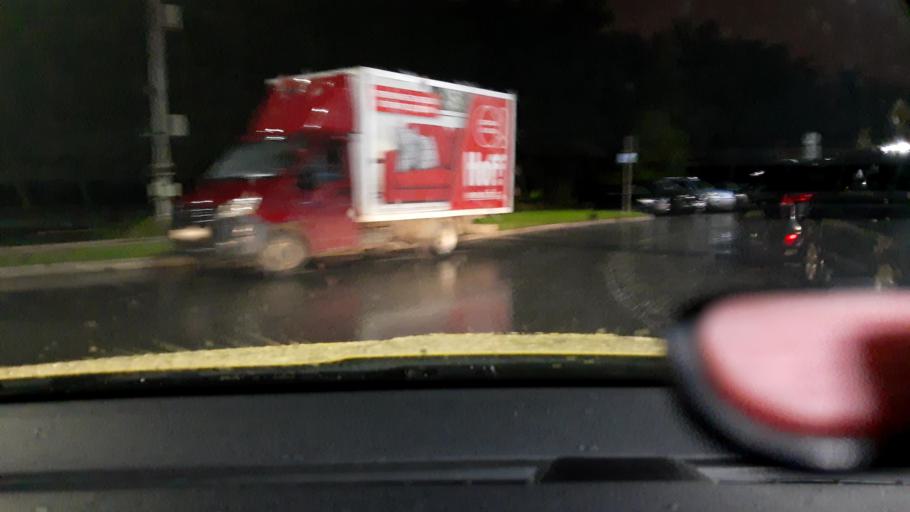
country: RU
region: Moscow
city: Zhulebino
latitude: 55.6690
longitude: 37.8549
